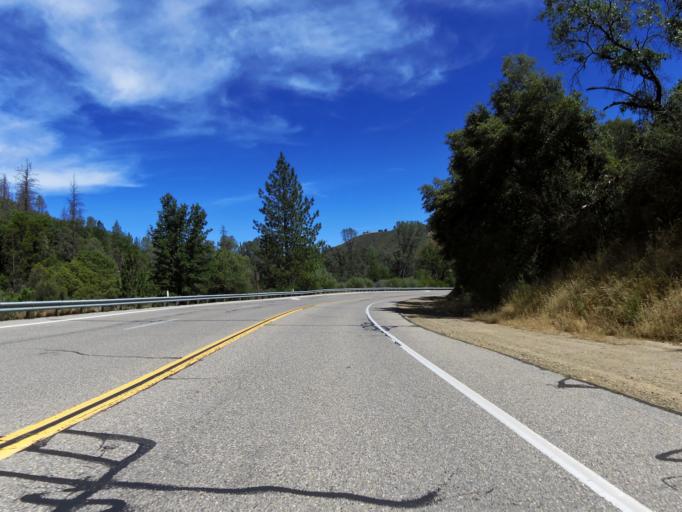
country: US
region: California
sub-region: Mariposa County
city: Midpines
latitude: 37.5692
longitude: -119.9427
